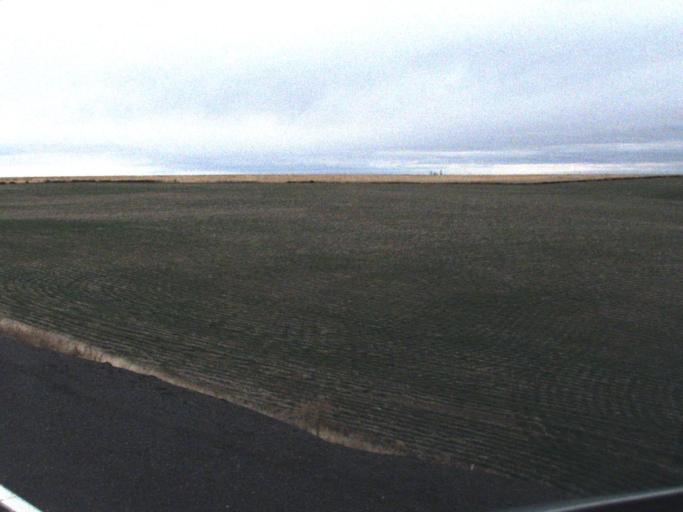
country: US
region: Washington
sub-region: Franklin County
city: Connell
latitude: 46.7948
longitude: -118.5553
